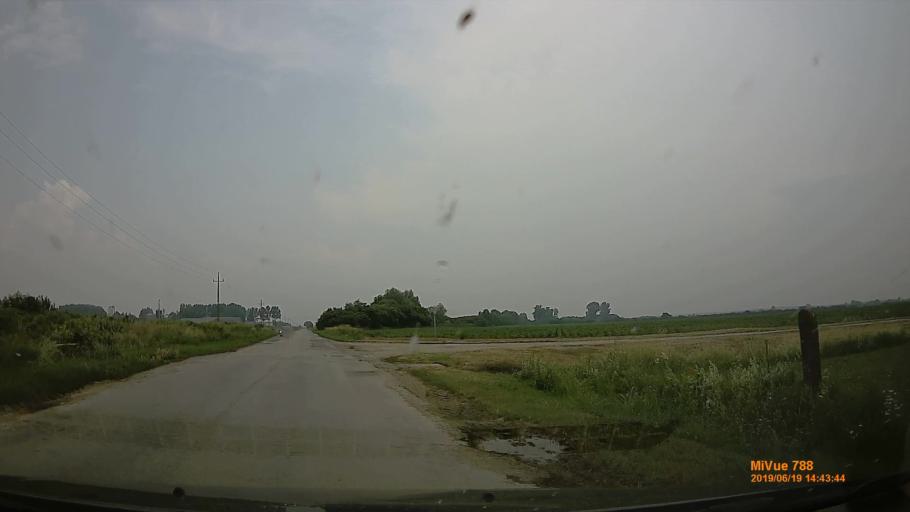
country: HU
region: Baranya
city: Szigetvar
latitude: 46.0365
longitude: 17.8216
